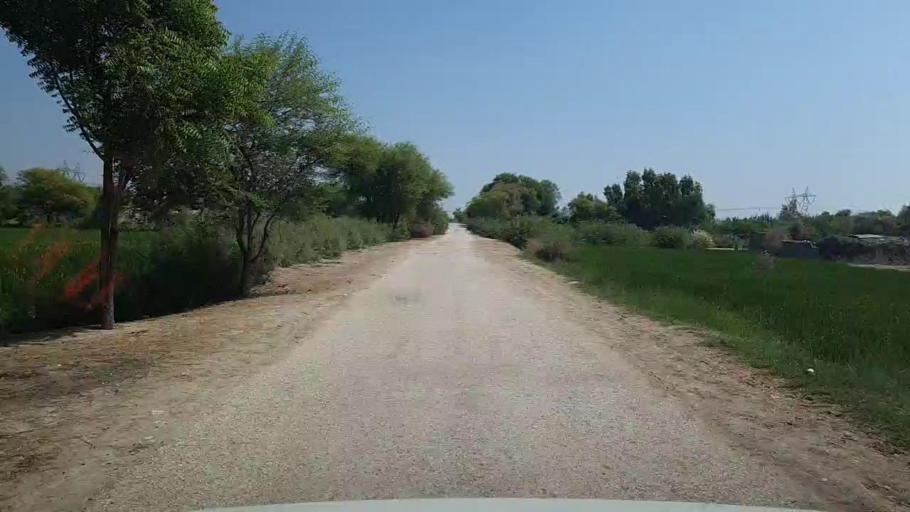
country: PK
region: Sindh
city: Kandhkot
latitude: 28.2893
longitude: 69.3528
